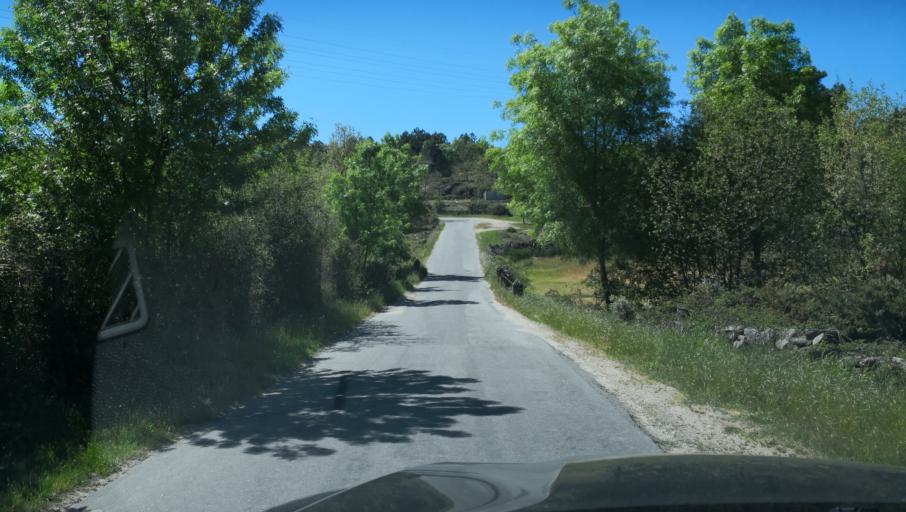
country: PT
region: Vila Real
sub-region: Vila Real
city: Vila Real
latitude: 41.2938
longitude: -7.6654
